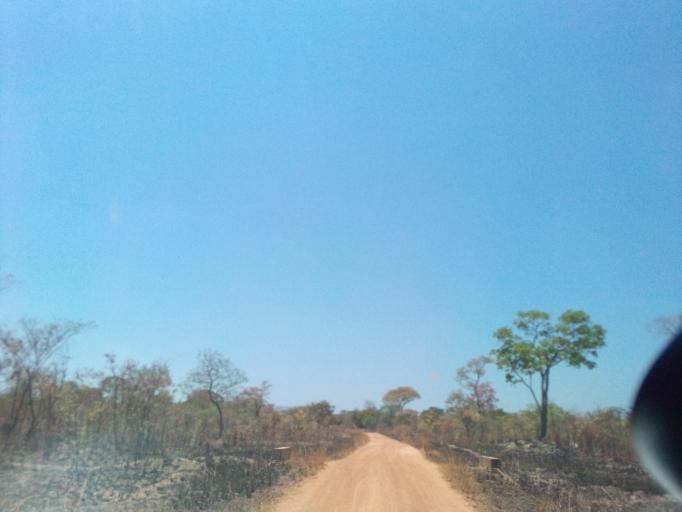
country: ZM
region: Northern
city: Mpika
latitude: -12.2529
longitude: 30.6778
